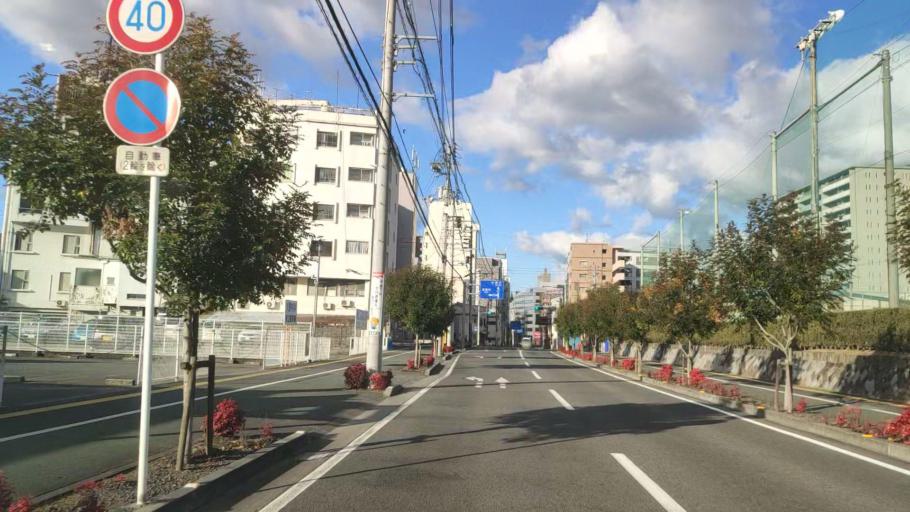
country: JP
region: Ehime
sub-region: Shikoku-chuo Shi
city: Matsuyama
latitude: 33.8414
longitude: 132.7792
